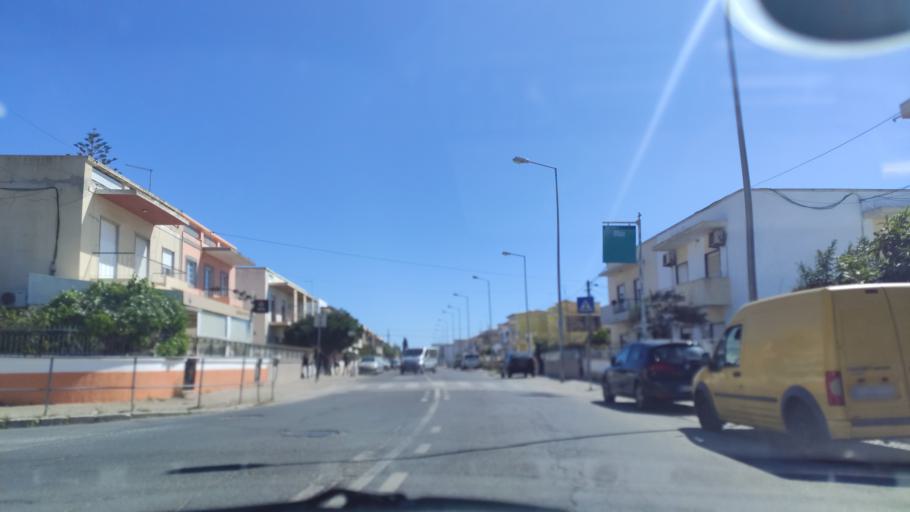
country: PT
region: Faro
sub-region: Olhao
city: Olhao
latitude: 37.0376
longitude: -7.8501
